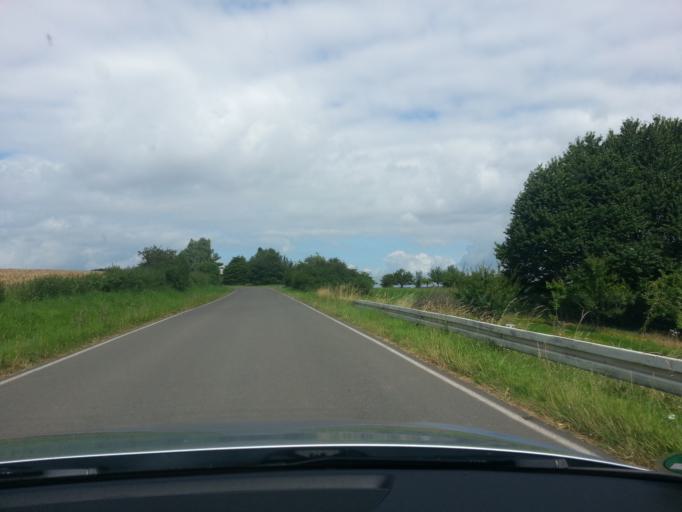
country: DE
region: Saarland
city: Orscholz
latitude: 49.5255
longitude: 6.5066
